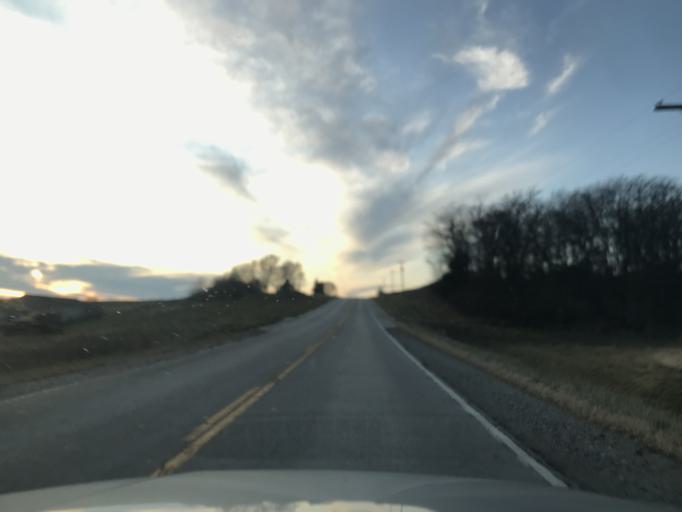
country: US
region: Illinois
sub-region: Henderson County
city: Oquawka
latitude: 41.0189
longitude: -90.8279
